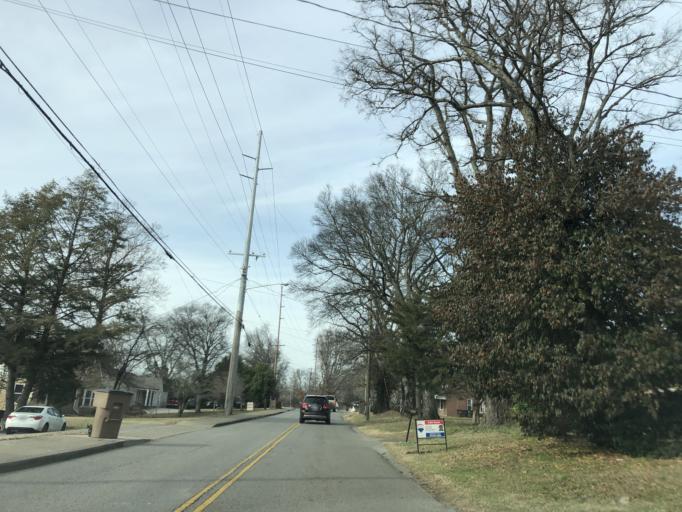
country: US
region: Tennessee
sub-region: Davidson County
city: Nashville
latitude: 36.2119
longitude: -86.7203
